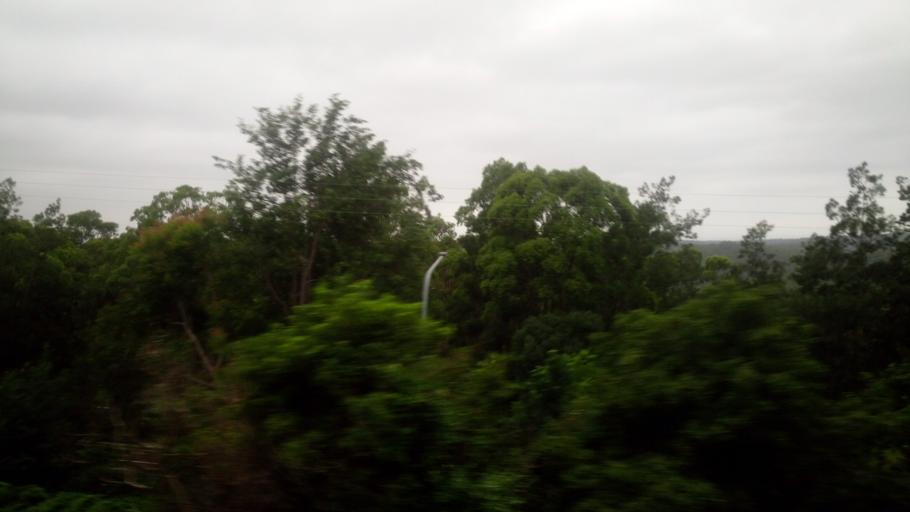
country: AU
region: New South Wales
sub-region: Blue Mountains Municipality
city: Blaxland
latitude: -33.7095
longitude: 150.5858
